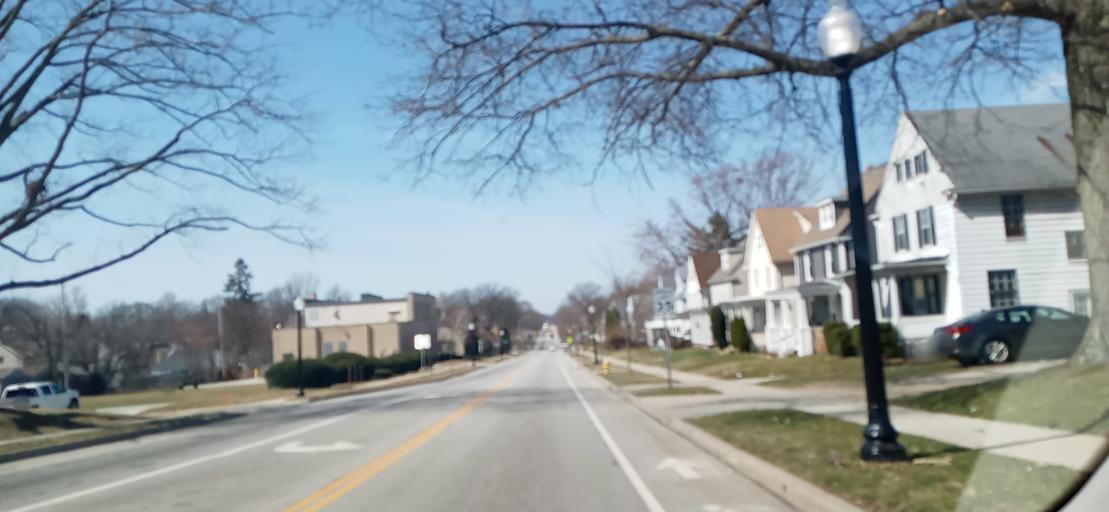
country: US
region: Ohio
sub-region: Summit County
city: Portage Lakes
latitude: 41.0399
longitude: -81.5106
